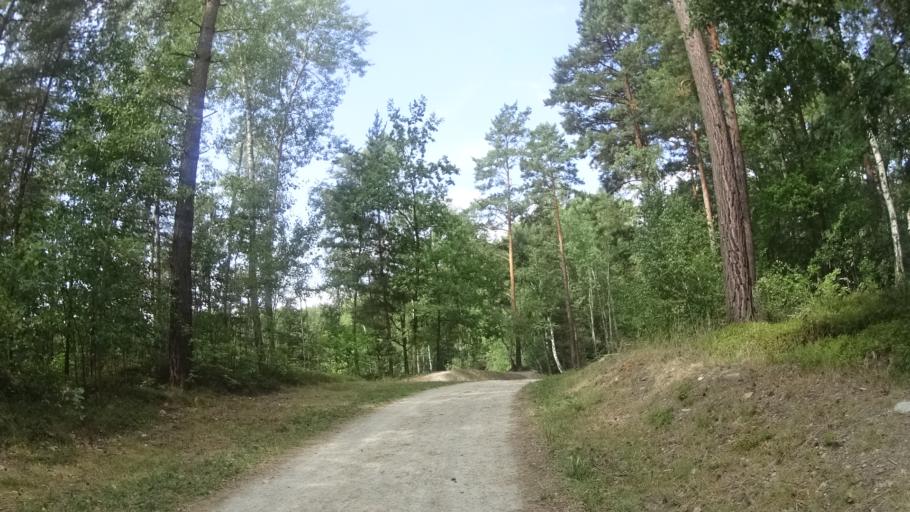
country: PL
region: Lubusz
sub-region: Powiat zarski
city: Leknica
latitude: 51.5358
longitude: 14.7593
